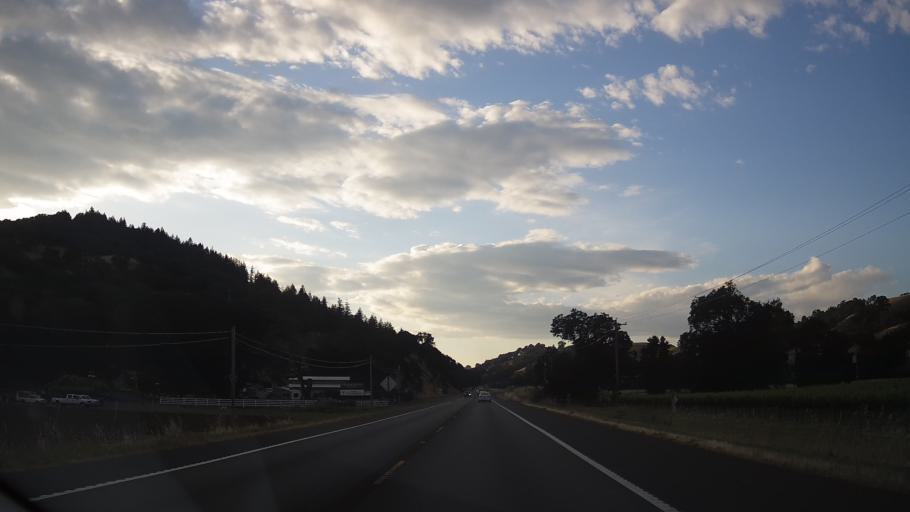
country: US
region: California
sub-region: Mendocino County
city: Talmage
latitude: 39.0528
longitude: -123.1562
